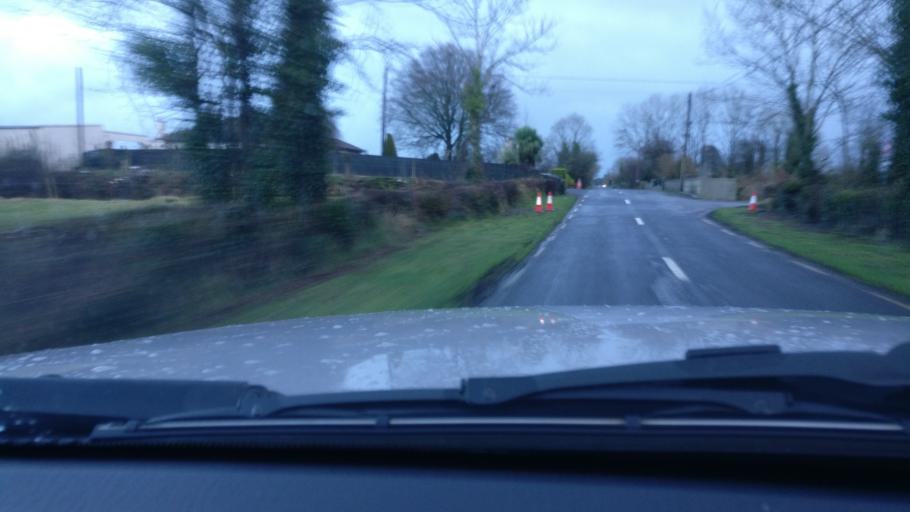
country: IE
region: Connaught
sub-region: County Galway
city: Ballinasloe
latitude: 53.2292
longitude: -8.3405
